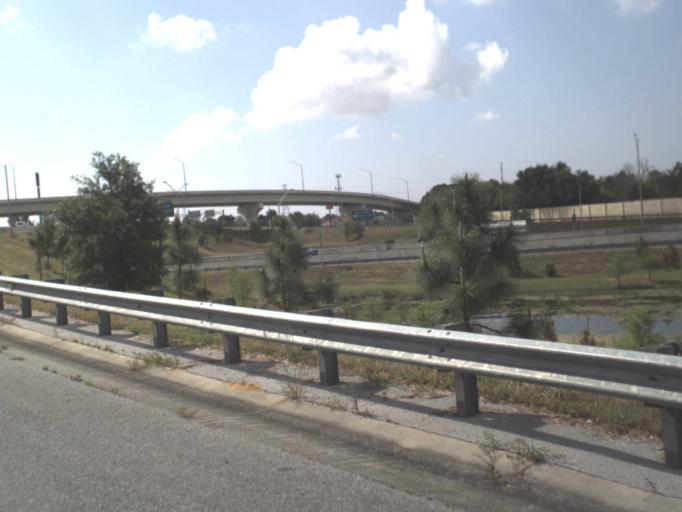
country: US
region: Florida
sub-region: Escambia County
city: Ferry Pass
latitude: 30.5049
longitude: -87.2316
